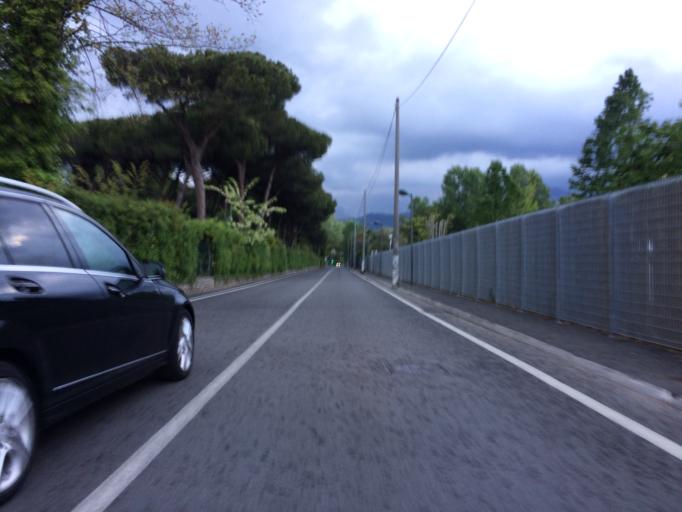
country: IT
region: Tuscany
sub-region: Provincia di Massa-Carrara
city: Carrara
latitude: 44.0285
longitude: 10.0698
